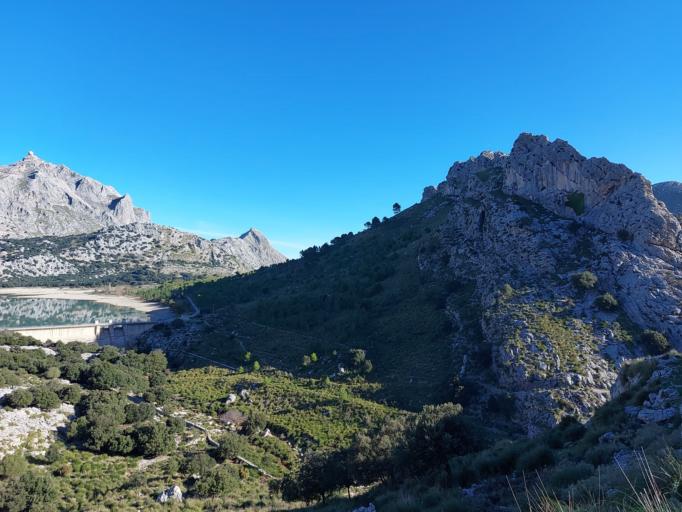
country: ES
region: Balearic Islands
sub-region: Illes Balears
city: Fornalutx
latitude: 39.7774
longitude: 2.7906
